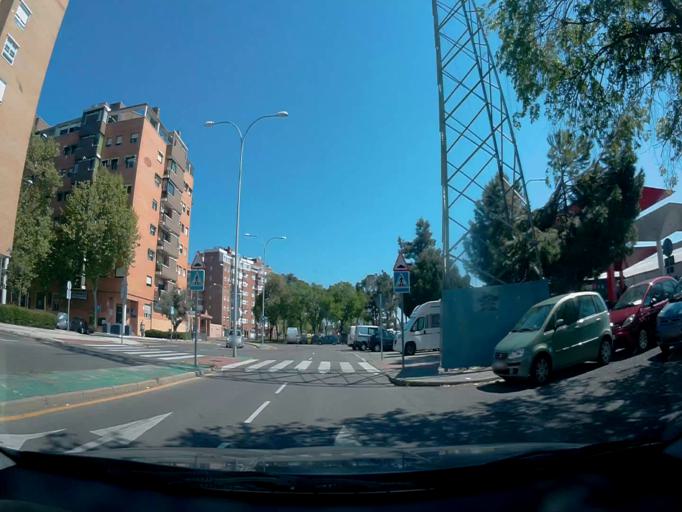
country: ES
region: Madrid
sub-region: Provincia de Madrid
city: Alcorcon
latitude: 40.3462
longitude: -3.8060
